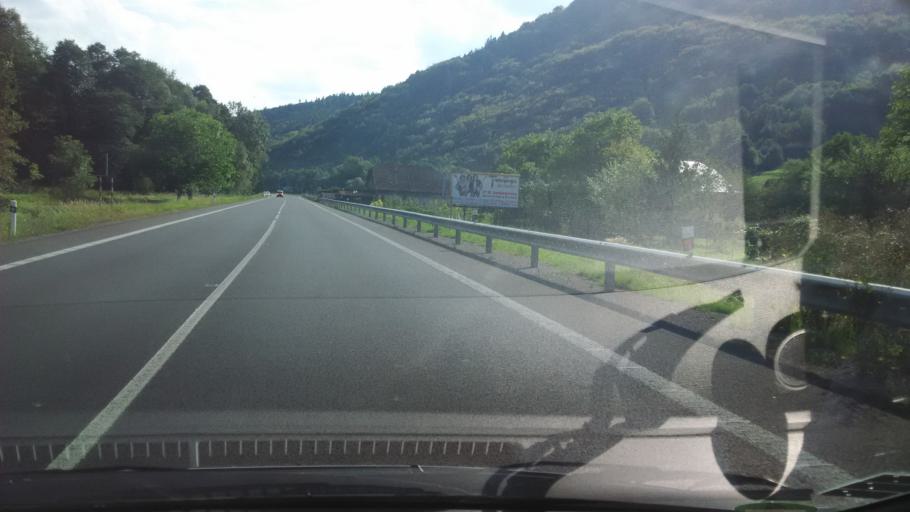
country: SK
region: Banskobystricky
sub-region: Okres Ziar nad Hronom
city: Kremnica
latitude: 48.6758
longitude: 18.9117
